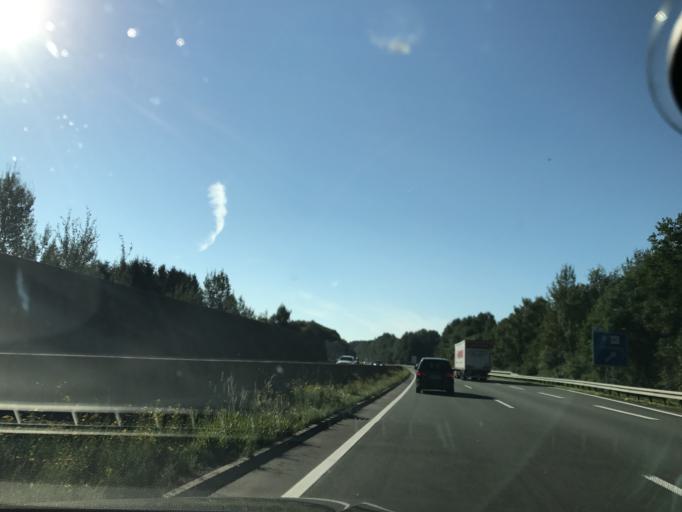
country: DE
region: North Rhine-Westphalia
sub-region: Regierungsbezirk Arnsberg
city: Wenden
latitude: 50.9373
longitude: 7.8800
